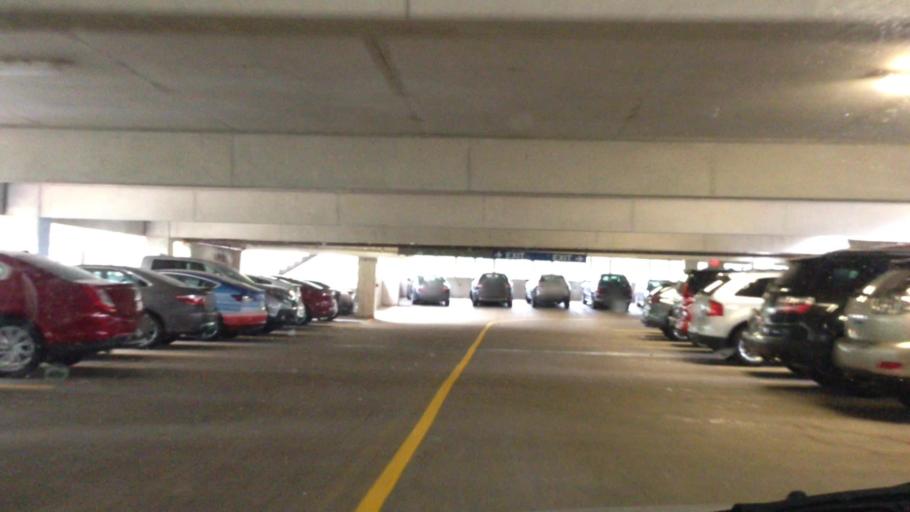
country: US
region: Minnesota
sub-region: Hennepin County
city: Saint Louis Park
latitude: 44.9278
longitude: -93.3615
